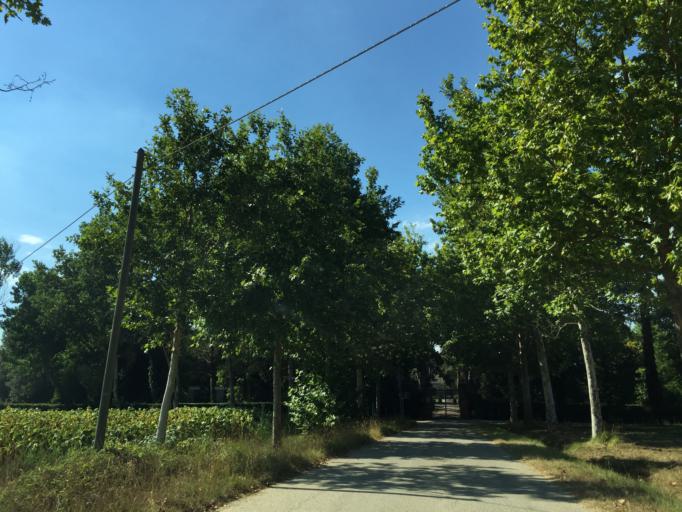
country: IT
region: Tuscany
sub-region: Provincia di Pistoia
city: Uggia-Pazzera-Bizzarrino
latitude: 43.8211
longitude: 10.8327
